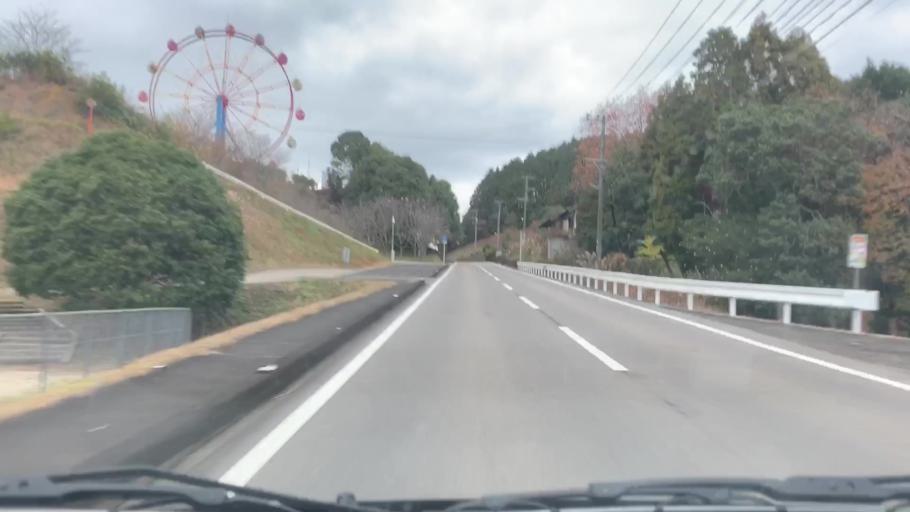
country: JP
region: Saga Prefecture
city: Ureshinomachi-shimojuku
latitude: 33.1297
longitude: 129.9778
